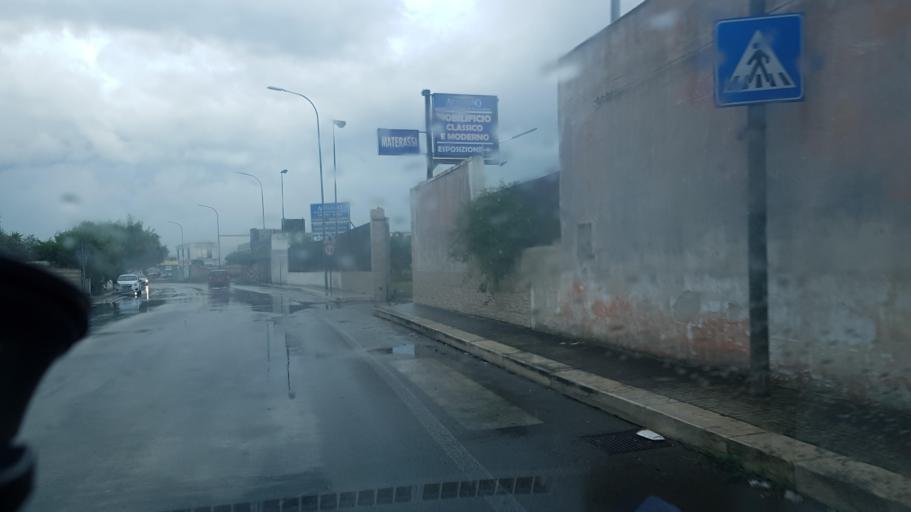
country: IT
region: Apulia
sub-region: Provincia di Lecce
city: Surbo
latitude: 40.3822
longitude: 18.1374
